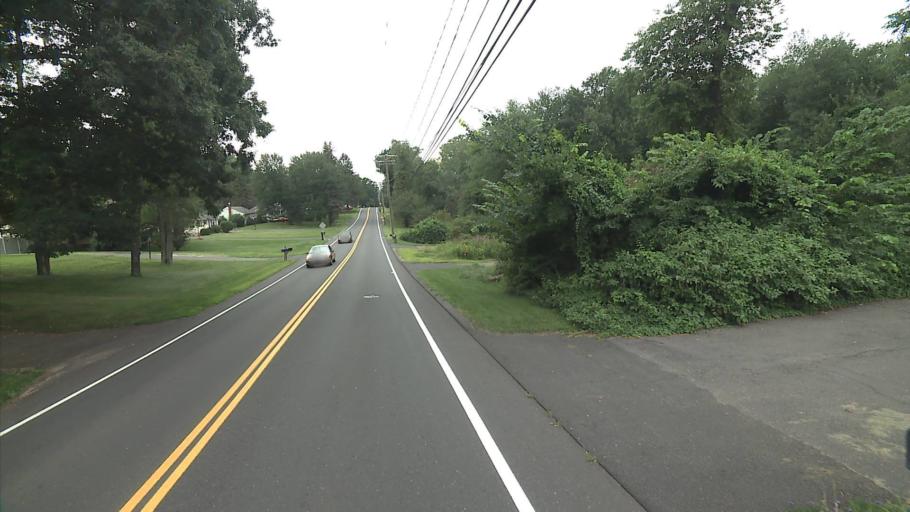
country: US
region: Connecticut
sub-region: Hartford County
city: Manchester
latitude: 41.8396
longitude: -72.5354
